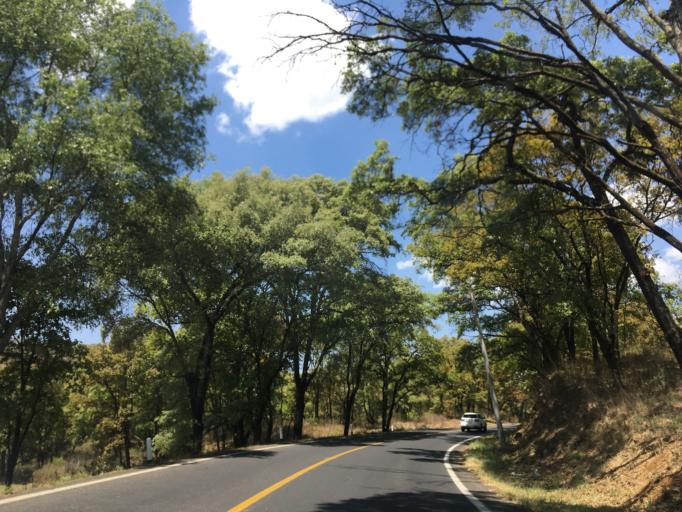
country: MX
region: Michoacan
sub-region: Chilchota
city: Tacuro (Santa Maria Tacuro)
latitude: 19.8091
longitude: -102.0266
